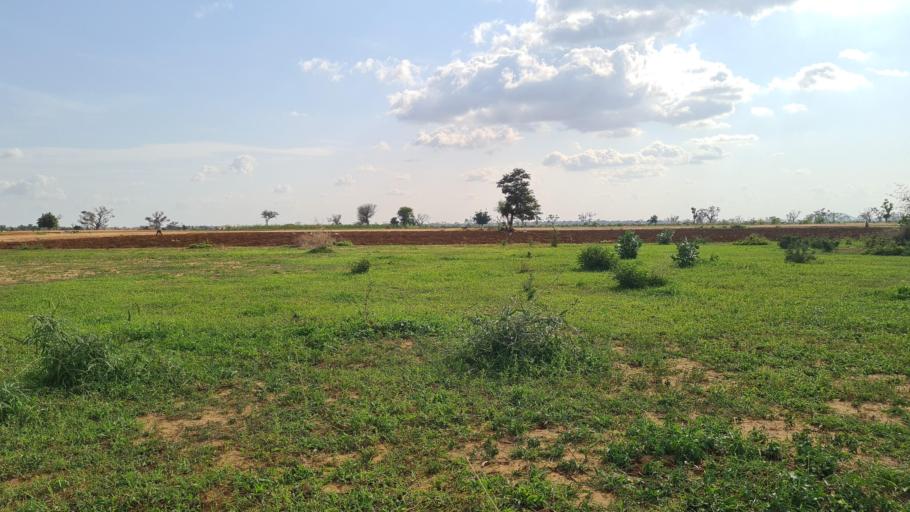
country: NE
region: Tahoua
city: Birni N Konni
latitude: 13.8114
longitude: 5.2809
